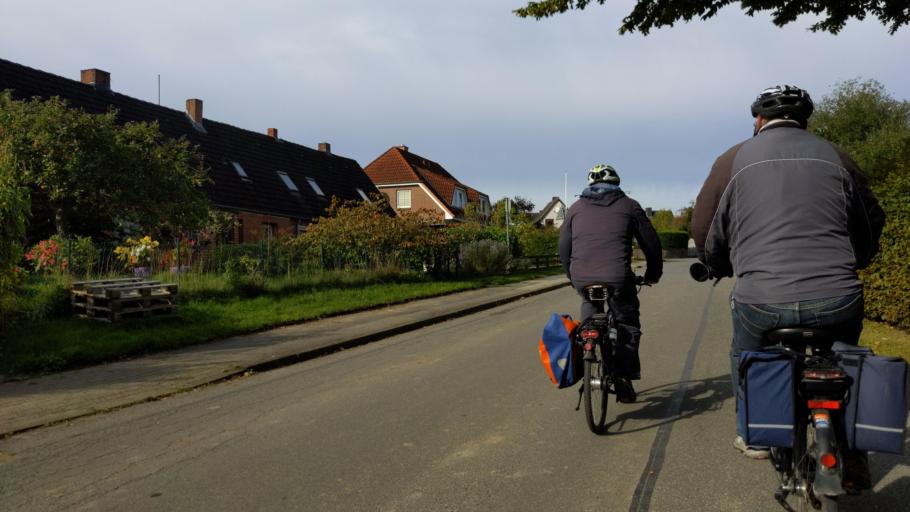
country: DE
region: Schleswig-Holstein
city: Zarpen
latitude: 53.8743
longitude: 10.5142
